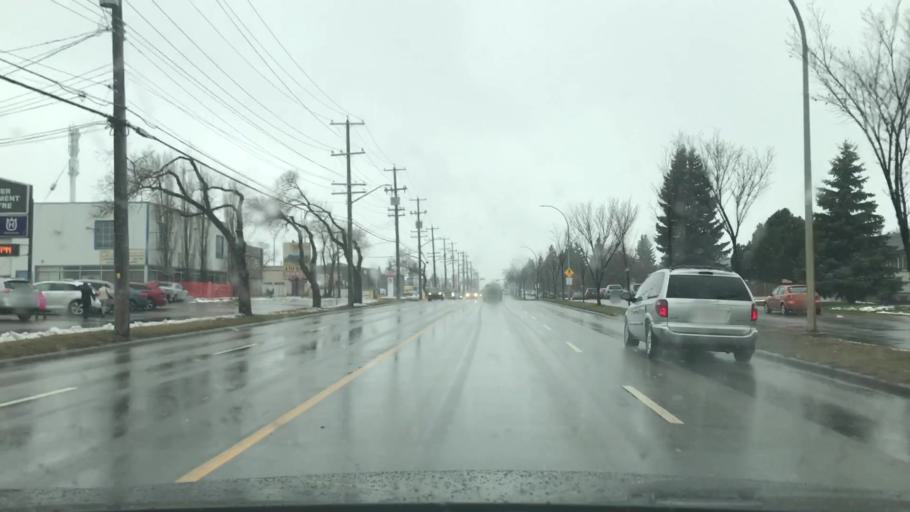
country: CA
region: Alberta
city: Edmonton
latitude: 53.4999
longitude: -113.4739
